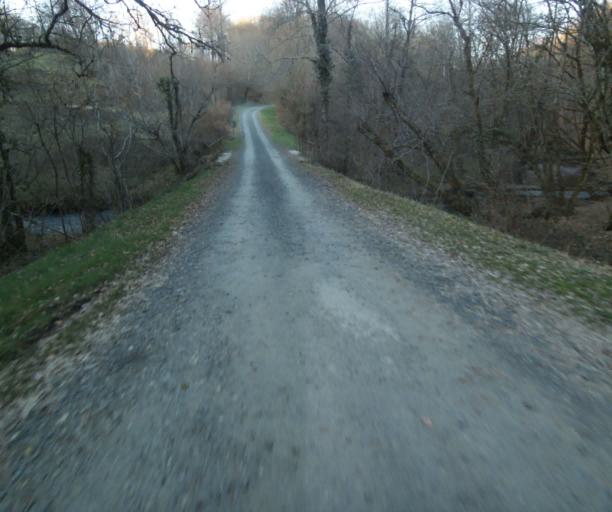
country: FR
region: Limousin
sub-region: Departement de la Correze
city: Uzerche
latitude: 45.3520
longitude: 1.6000
